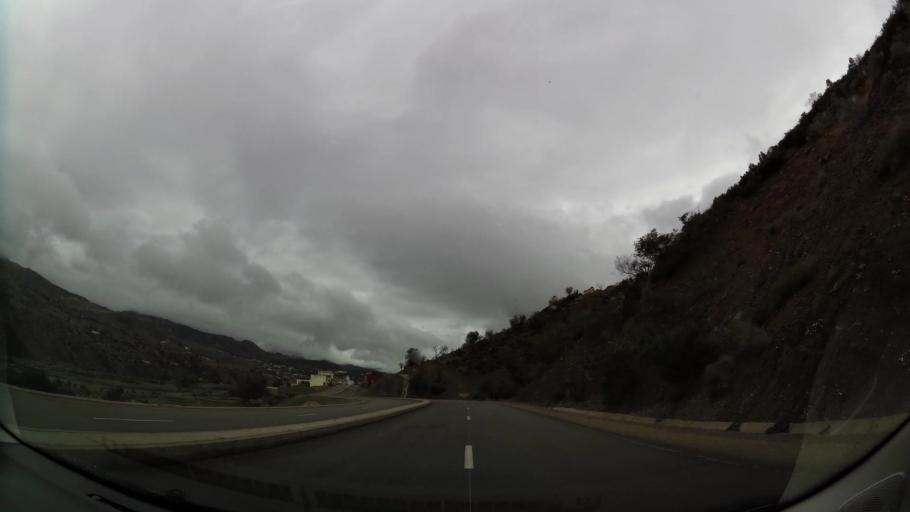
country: MA
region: Taza-Al Hoceima-Taounate
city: Imzourene
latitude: 34.9725
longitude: -3.8138
